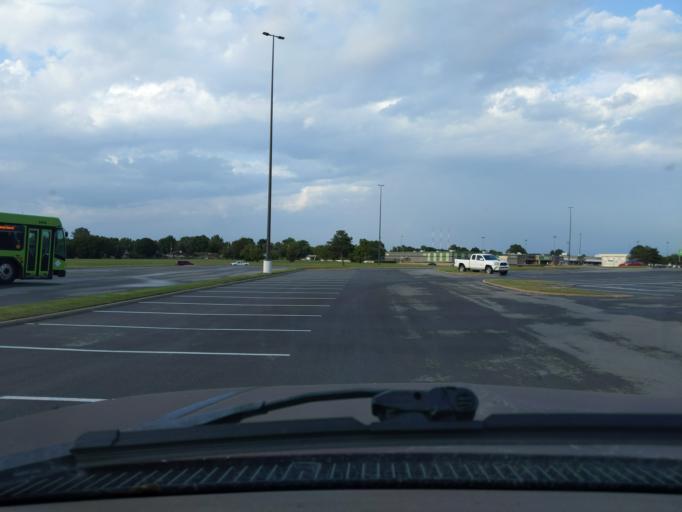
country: US
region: Oklahoma
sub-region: Tulsa County
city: Broken Arrow
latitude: 36.1321
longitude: -95.8229
